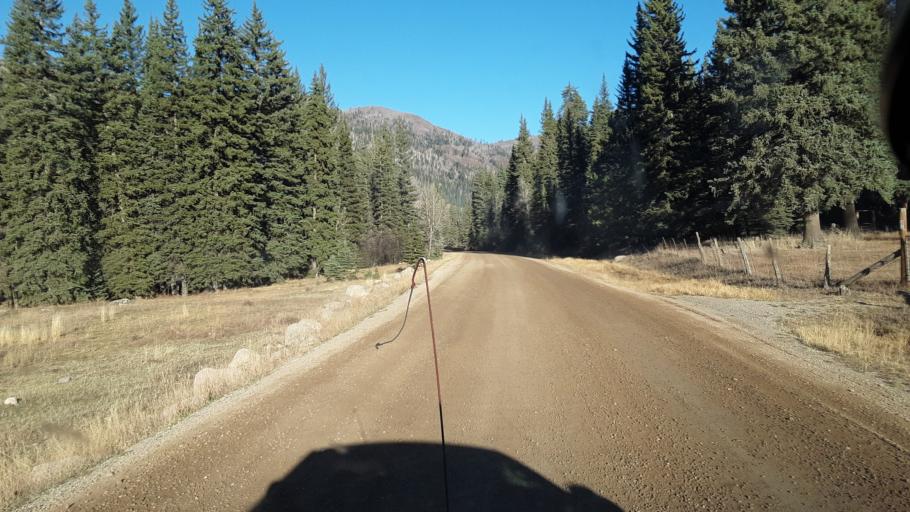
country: US
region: Colorado
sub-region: La Plata County
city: Bayfield
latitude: 37.4237
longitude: -107.6704
